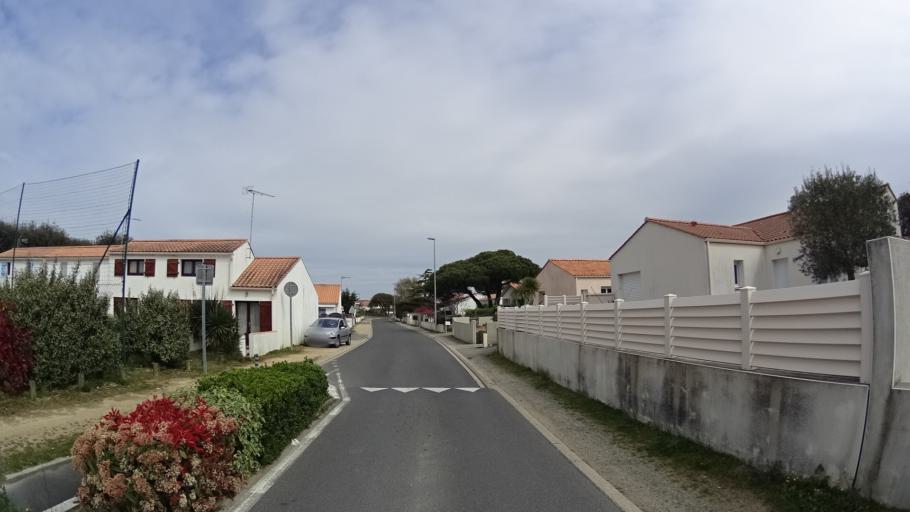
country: FR
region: Pays de la Loire
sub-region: Departement de la Vendee
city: La Barre-de-Monts
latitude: 46.8877
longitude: -2.1213
